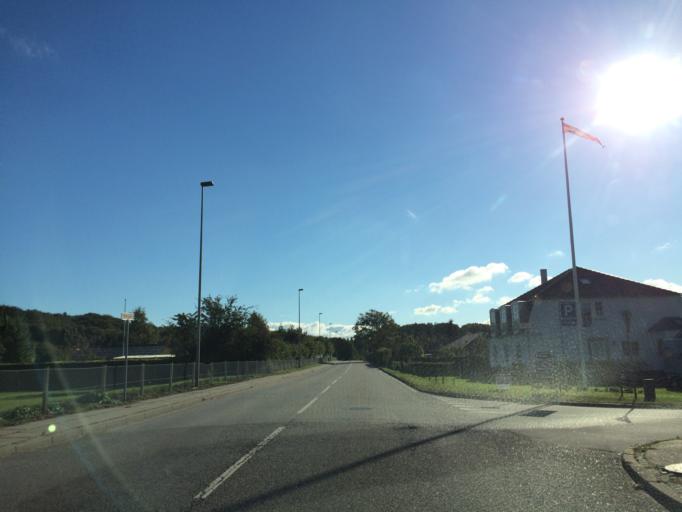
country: DK
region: Central Jutland
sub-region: Randers Kommune
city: Langa
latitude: 56.3560
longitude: 9.9197
